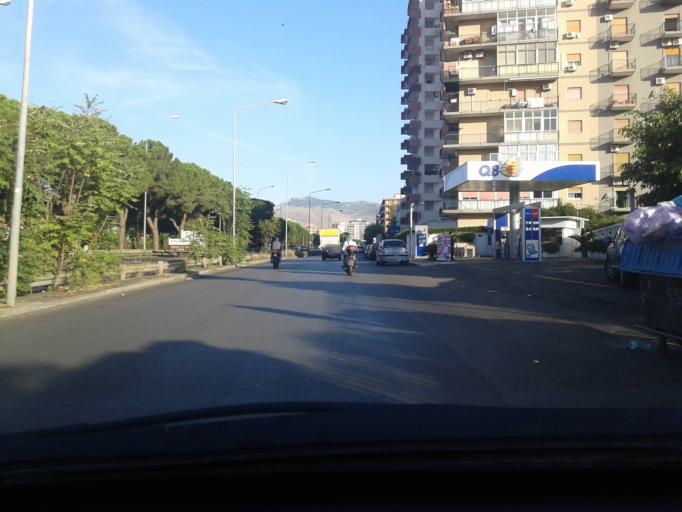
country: IT
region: Sicily
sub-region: Palermo
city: Palermo
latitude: 38.0971
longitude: 13.3352
